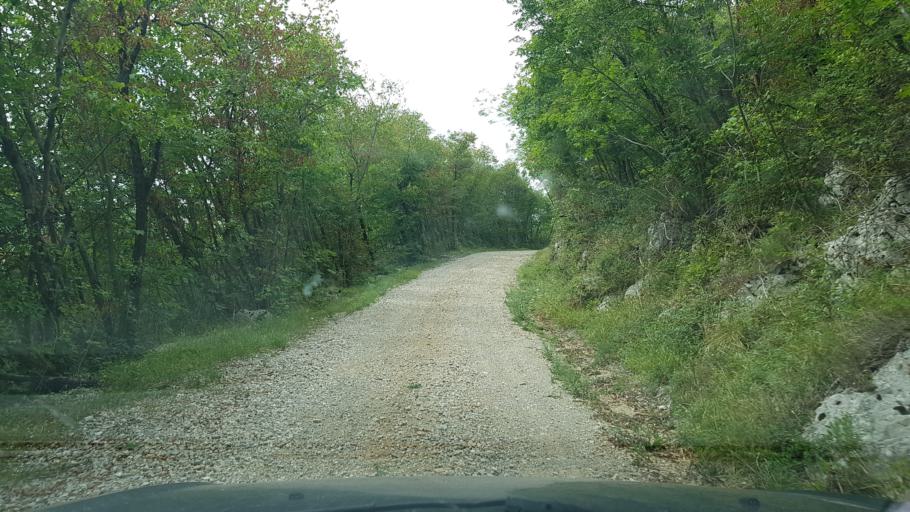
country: SI
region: Kanal
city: Deskle
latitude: 46.0169
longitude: 13.6213
